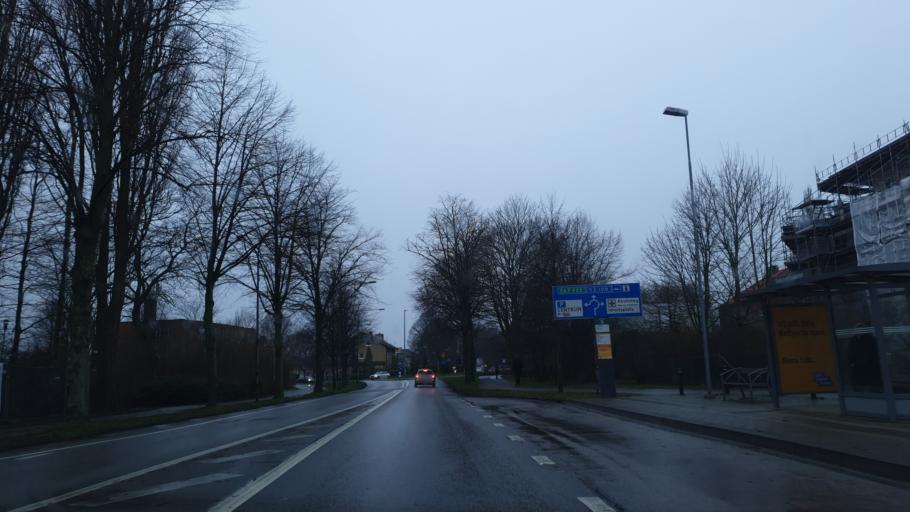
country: SE
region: Skane
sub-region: Trelleborgs Kommun
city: Trelleborg
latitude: 55.3802
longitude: 13.1603
